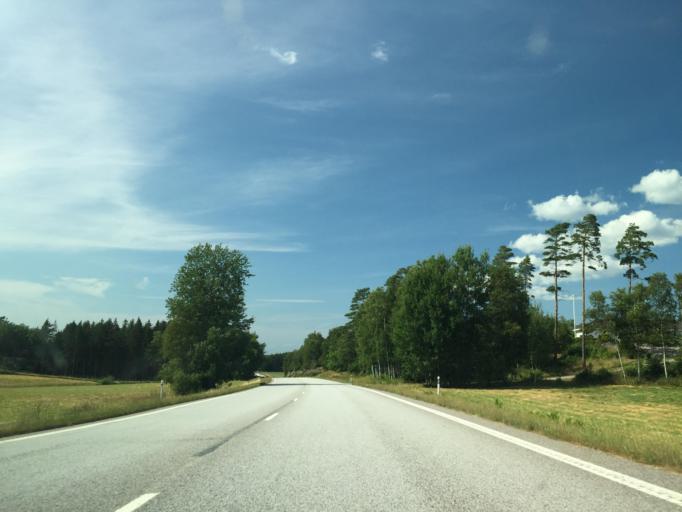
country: SE
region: Vaestra Goetaland
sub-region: Tanums Kommun
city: Tanumshede
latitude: 58.7560
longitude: 11.2783
